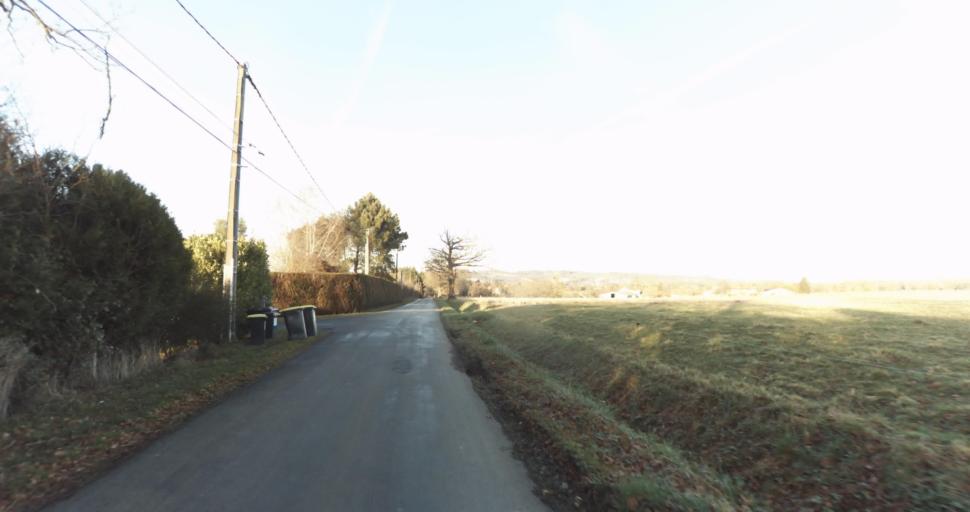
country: FR
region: Limousin
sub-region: Departement de la Haute-Vienne
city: Aixe-sur-Vienne
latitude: 45.7811
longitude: 1.1412
